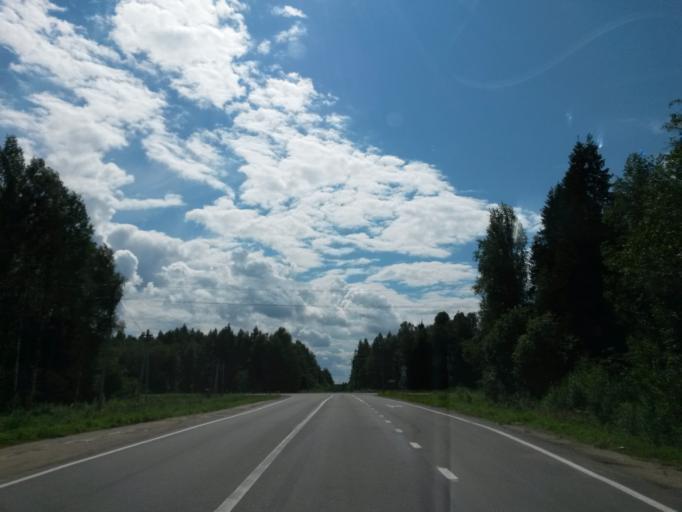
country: RU
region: Jaroslavl
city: Gavrilov-Yam
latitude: 57.2736
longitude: 39.9502
